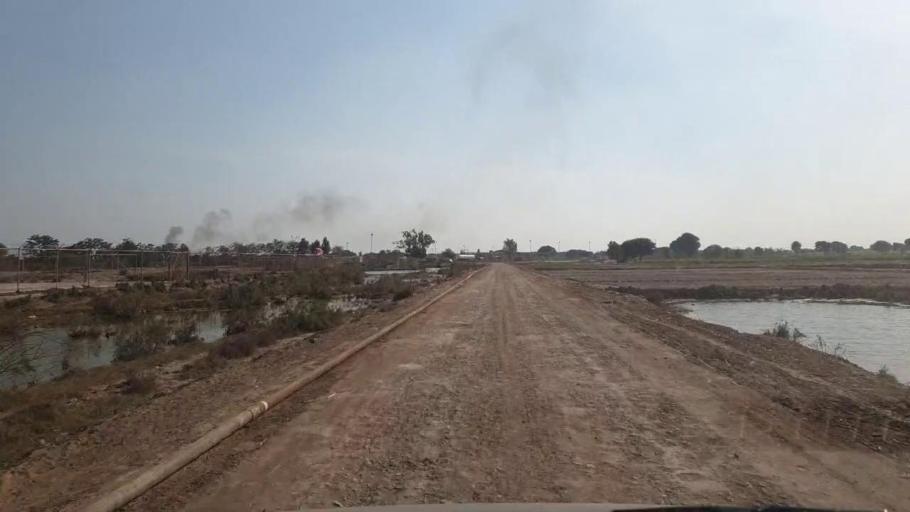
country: PK
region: Sindh
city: Chambar
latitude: 25.3289
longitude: 68.7738
